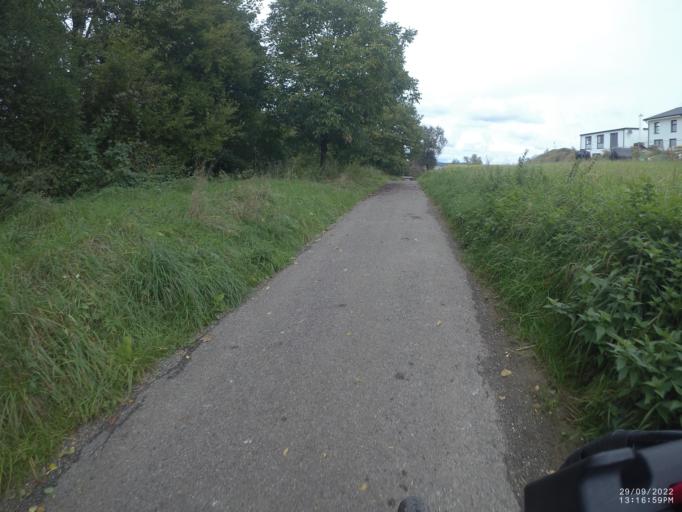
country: DE
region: Baden-Wuerttemberg
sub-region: Regierungsbezirk Stuttgart
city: Uhingen
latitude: 48.6973
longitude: 9.5849
